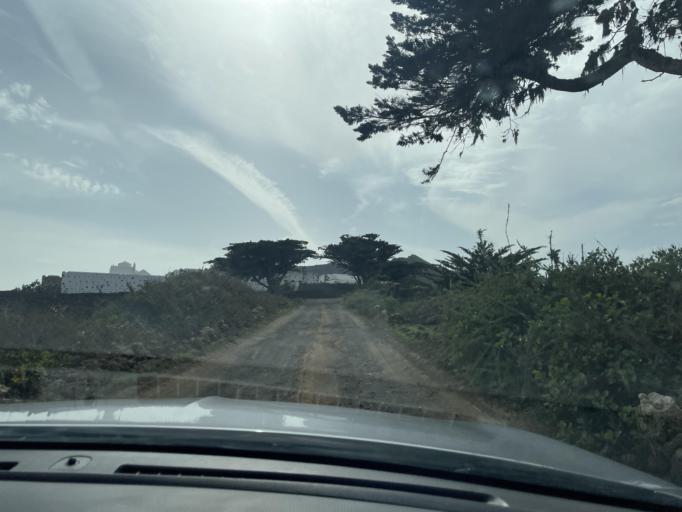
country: ES
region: Canary Islands
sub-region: Provincia de Las Palmas
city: Haria
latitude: 29.1937
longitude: -13.4748
